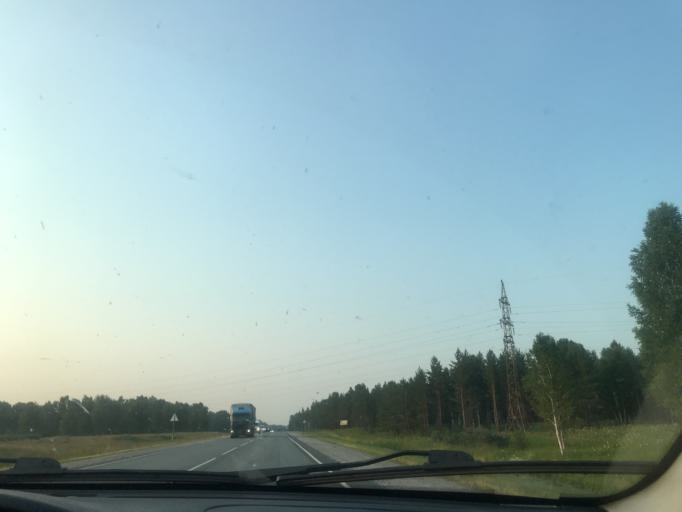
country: RU
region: Novosibirsk
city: Dorogino
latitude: 54.3761
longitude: 83.3059
